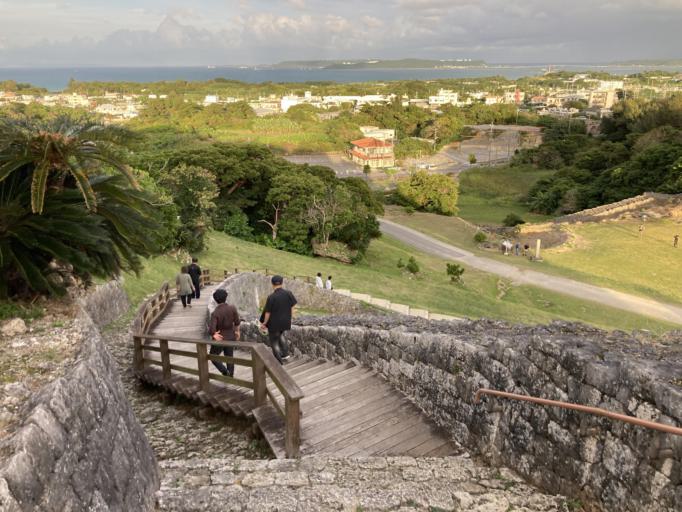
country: JP
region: Okinawa
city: Katsuren-haebaru
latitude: 26.3303
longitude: 127.8791
